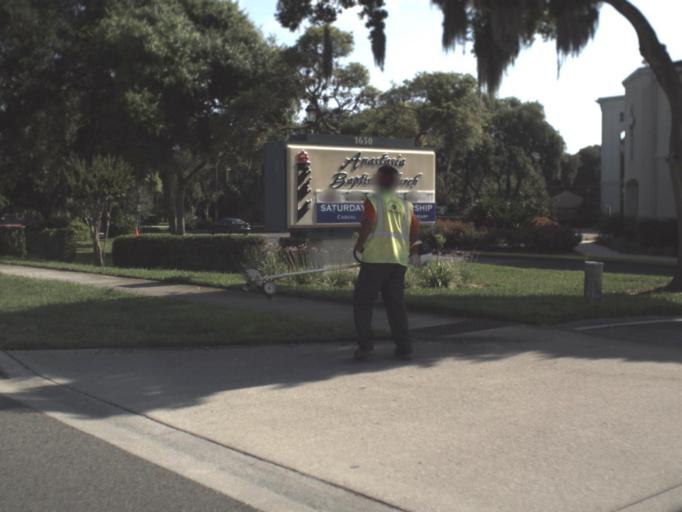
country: US
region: Florida
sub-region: Saint Johns County
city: Saint Augustine Beach
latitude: 29.8675
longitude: -81.2829
